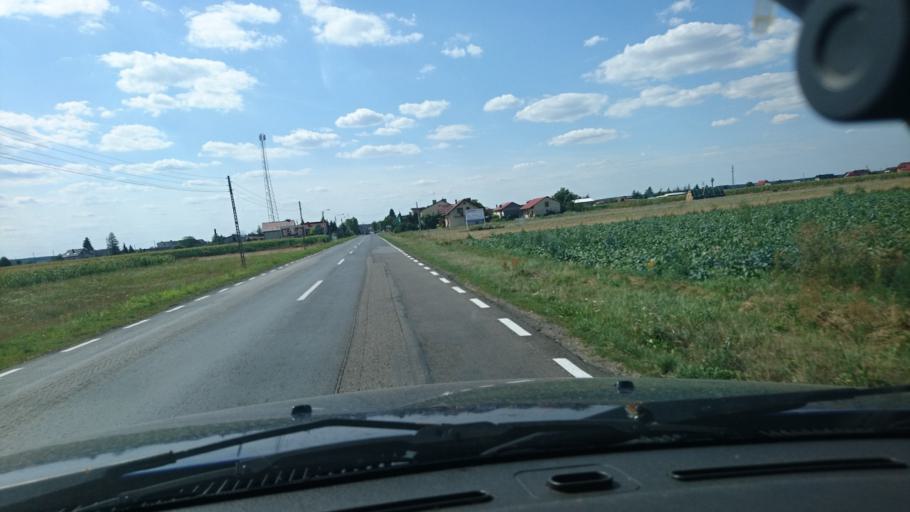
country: PL
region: Greater Poland Voivodeship
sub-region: Powiat krotoszynski
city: Sulmierzyce
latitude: 51.6055
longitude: 17.5461
